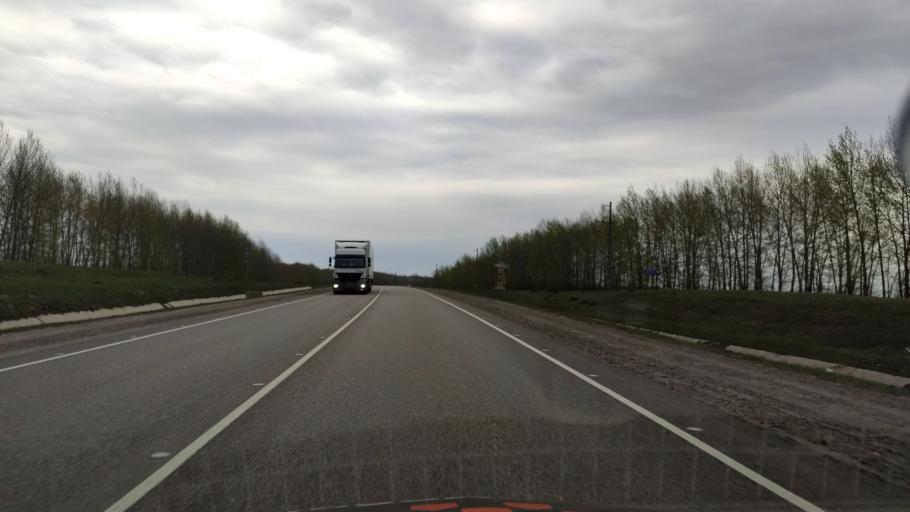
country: RU
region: Voronezj
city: Nizhnedevitsk
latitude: 51.5642
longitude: 38.4292
